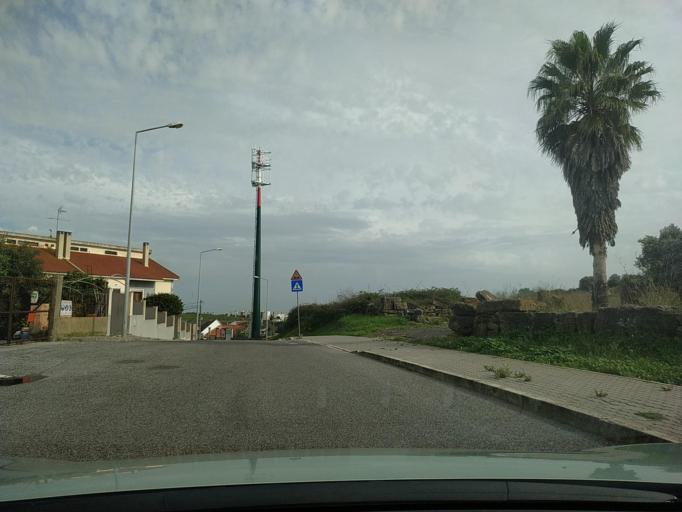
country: PT
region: Lisbon
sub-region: Amadora
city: Amadora
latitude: 38.7736
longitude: -9.2386
